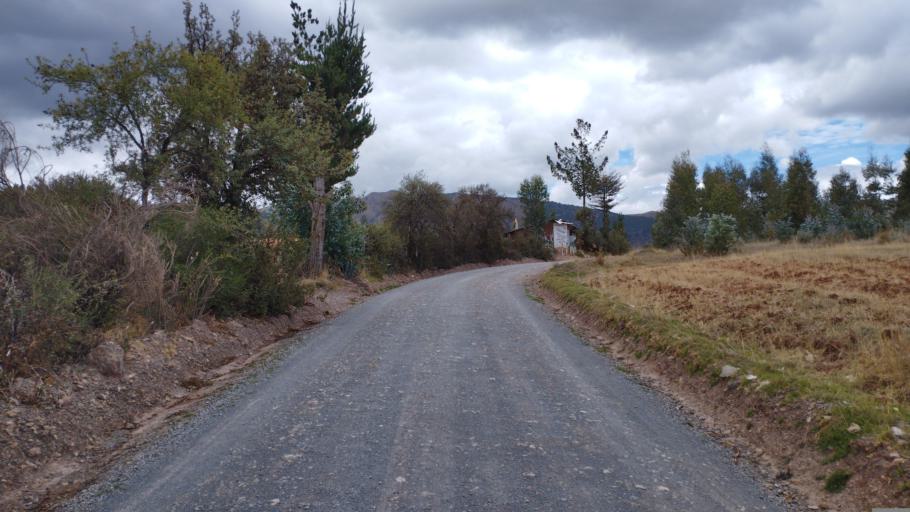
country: PE
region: Cusco
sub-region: Provincia de Cusco
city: Cusco
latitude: -13.5119
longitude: -71.9422
